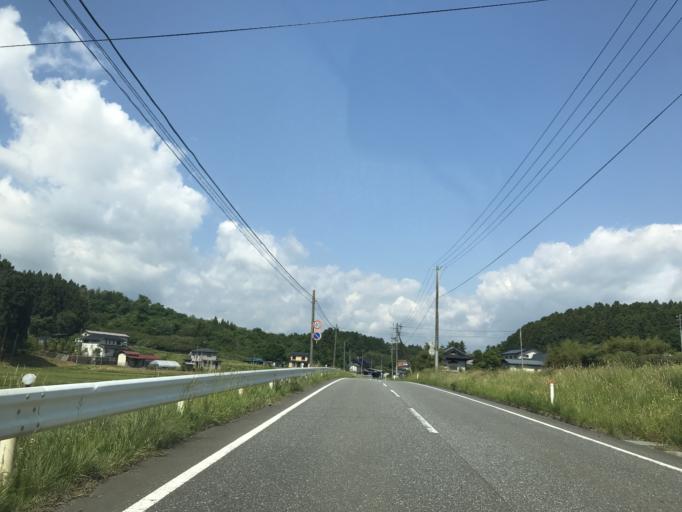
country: JP
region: Iwate
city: Ichinoseki
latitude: 38.7956
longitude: 141.0355
